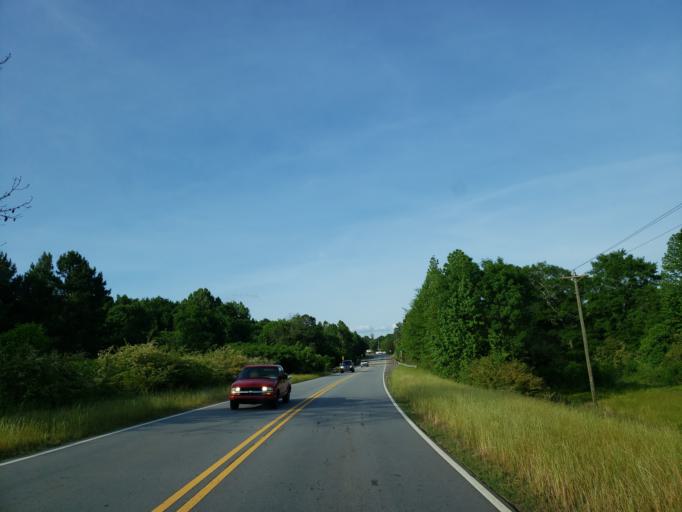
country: US
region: Georgia
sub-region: Carroll County
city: Bowdon
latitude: 33.4914
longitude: -85.2811
